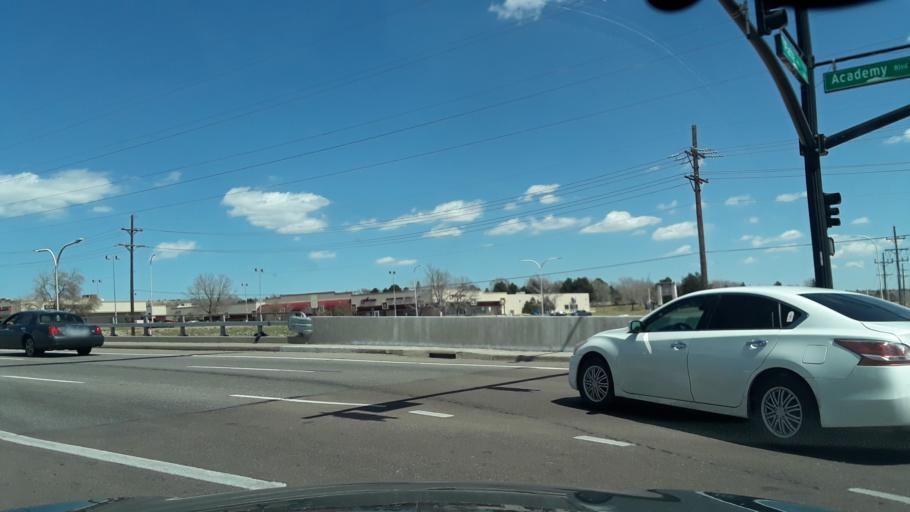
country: US
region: Colorado
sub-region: El Paso County
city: Cimarron Hills
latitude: 38.8393
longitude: -104.7574
